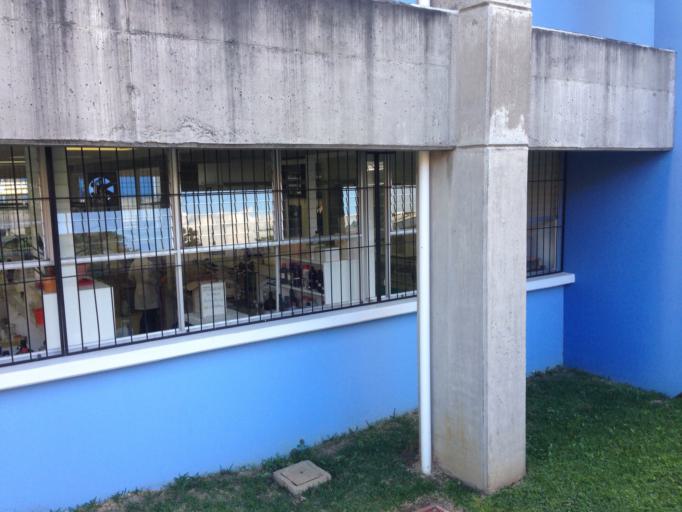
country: CR
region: San Jose
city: Sabanilla
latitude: 9.9398
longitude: -84.0433
